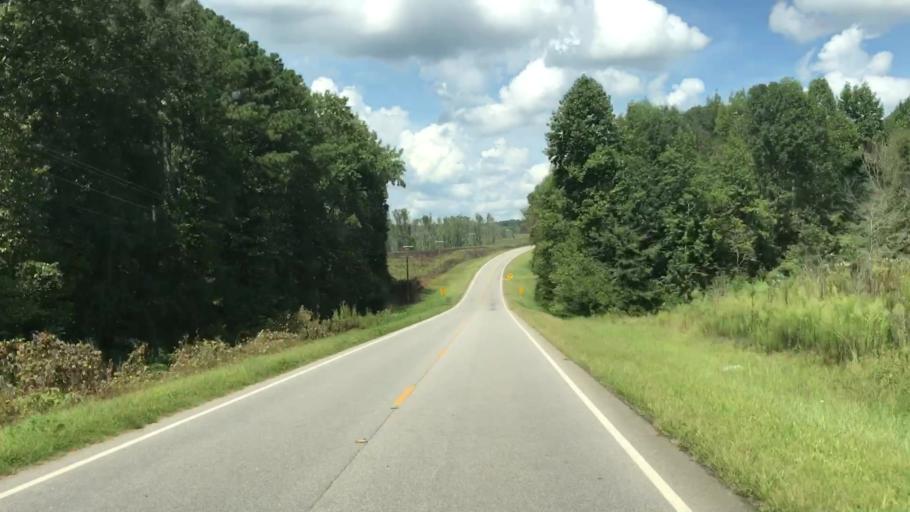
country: US
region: Georgia
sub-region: Greene County
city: Greensboro
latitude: 33.6097
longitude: -83.2044
